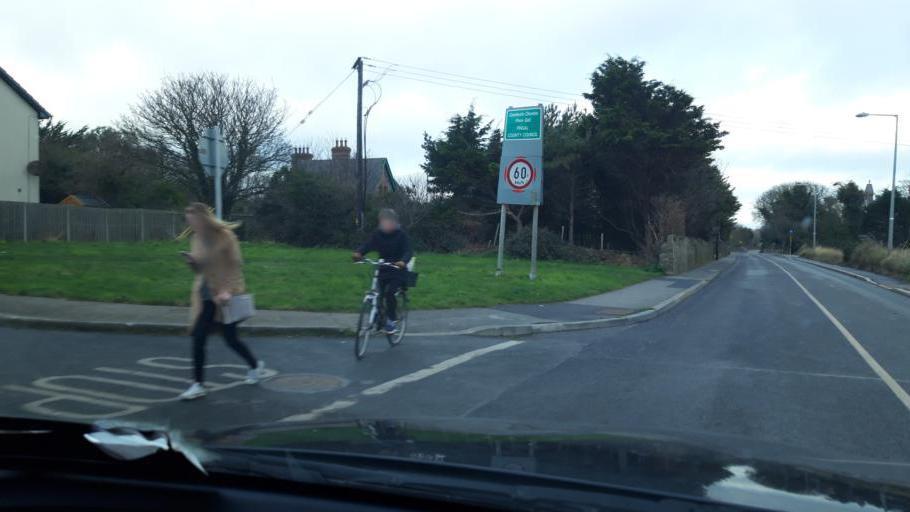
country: IE
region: Leinster
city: An Ros
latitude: 53.5279
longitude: -6.0912
